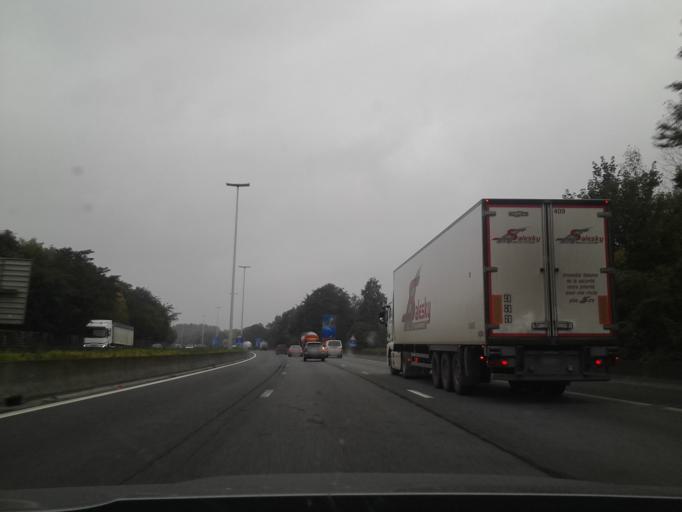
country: BE
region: Wallonia
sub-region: Province du Hainaut
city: Mons
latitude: 50.4786
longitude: 3.9392
